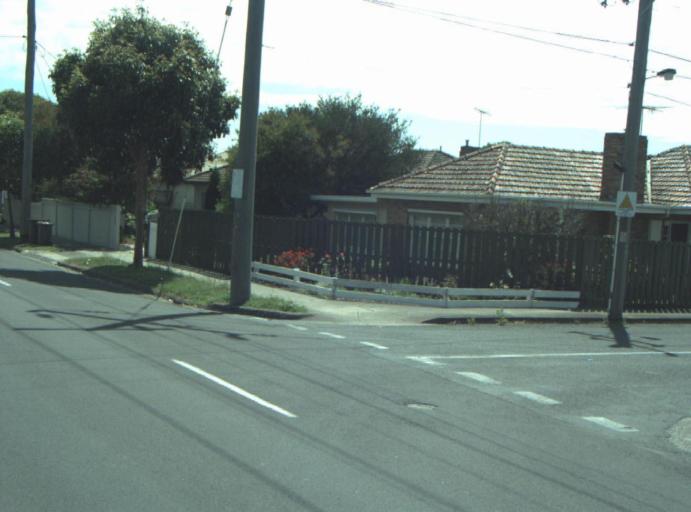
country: AU
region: Victoria
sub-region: Greater Geelong
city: Geelong West
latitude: -38.1320
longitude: 144.3380
